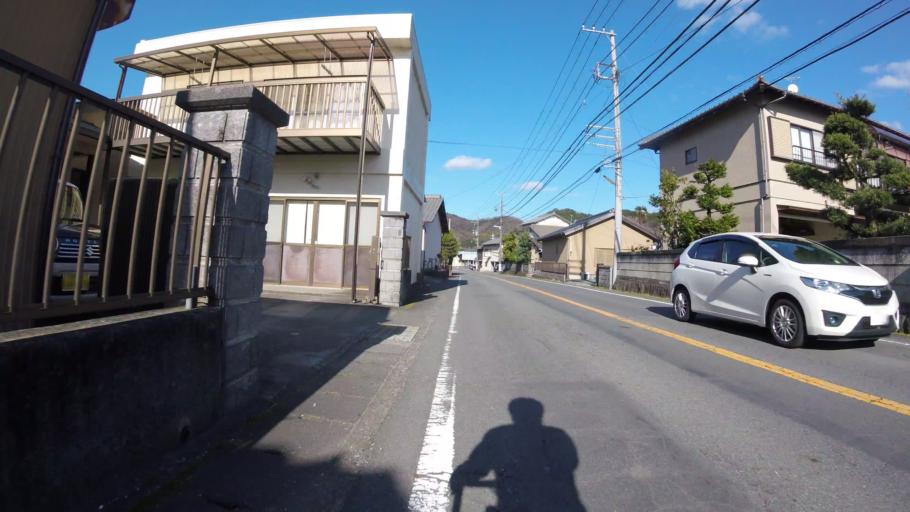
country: JP
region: Shizuoka
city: Ito
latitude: 34.9877
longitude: 138.9536
